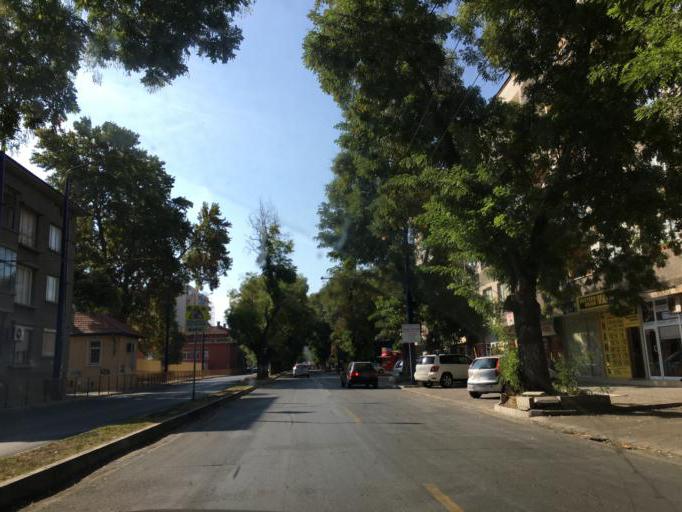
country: BG
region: Pazardzhik
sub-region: Obshtina Pazardzhik
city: Pazardzhik
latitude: 42.1989
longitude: 24.3332
